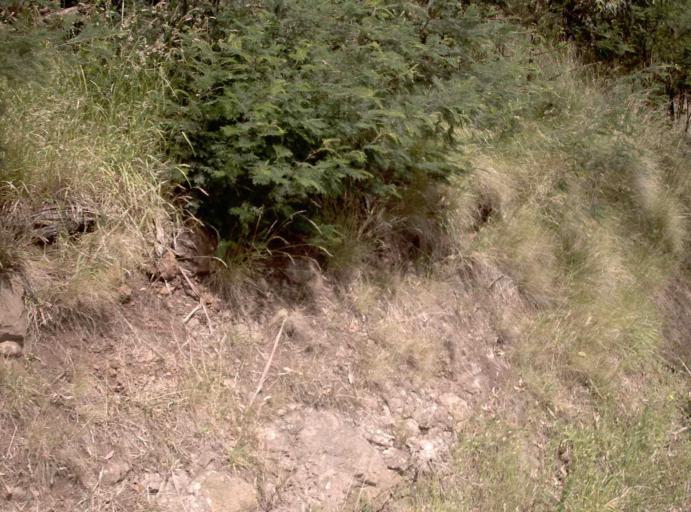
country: AU
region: Victoria
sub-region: Latrobe
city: Traralgon
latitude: -38.3287
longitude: 146.5749
